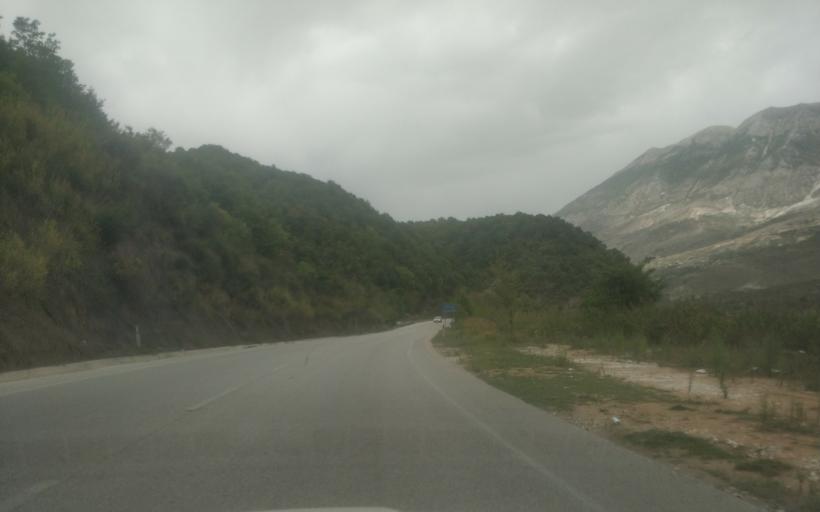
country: AL
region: Gjirokaster
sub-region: Rrethi i Gjirokastres
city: Picar
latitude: 40.2162
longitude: 20.0862
